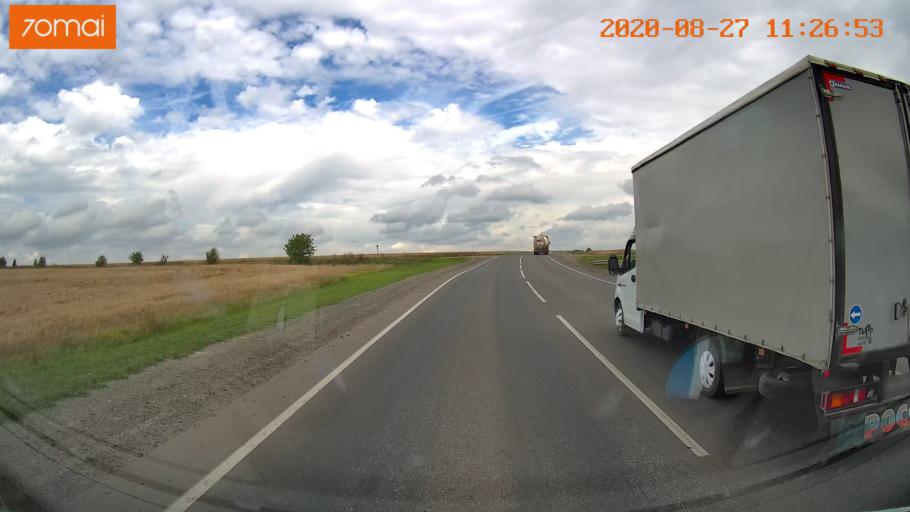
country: RU
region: Rjazan
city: Mikhaylov
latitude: 54.2425
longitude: 38.9863
